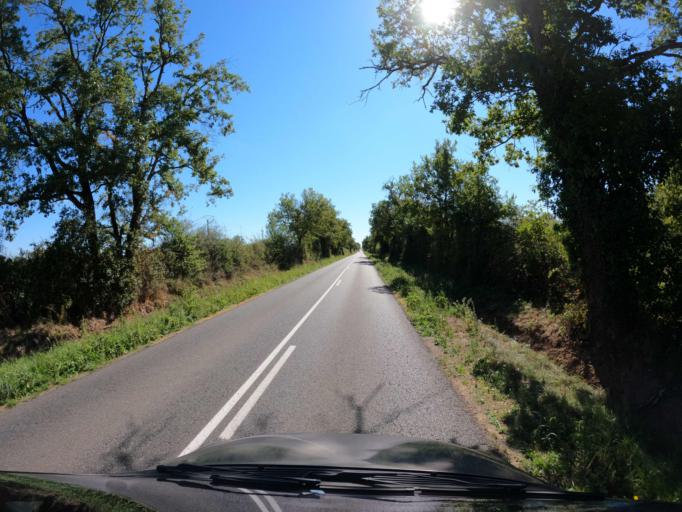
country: FR
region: Poitou-Charentes
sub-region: Departement de la Vienne
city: Saulge
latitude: 46.3900
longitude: 0.9089
